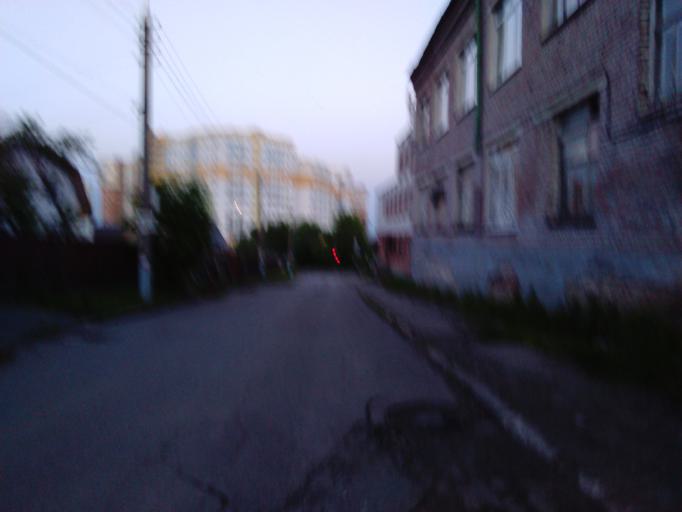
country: RU
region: Penza
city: Penza
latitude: 53.1747
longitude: 44.9980
